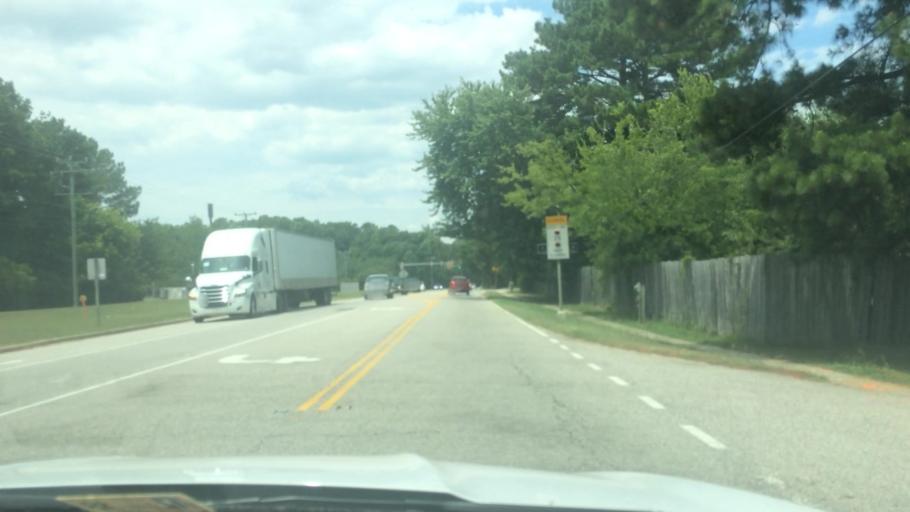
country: US
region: Virginia
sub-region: York County
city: Yorktown
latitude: 37.2092
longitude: -76.6140
